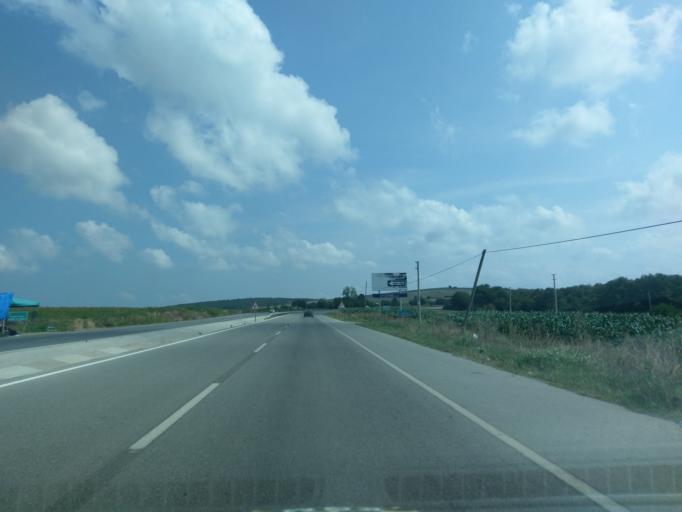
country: TR
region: Samsun
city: Bafra
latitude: 41.6021
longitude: 35.8270
